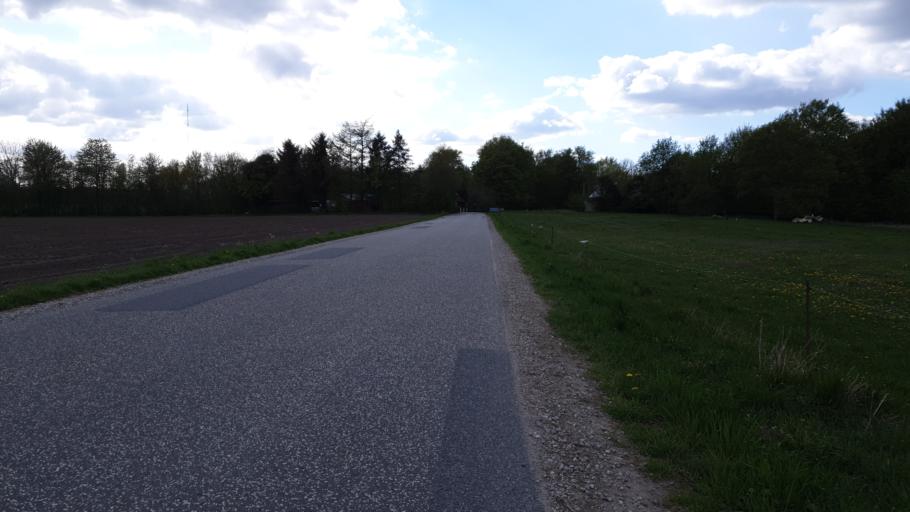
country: DK
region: Central Jutland
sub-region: Hedensted Kommune
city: Hedensted
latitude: 55.8117
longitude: 9.6630
